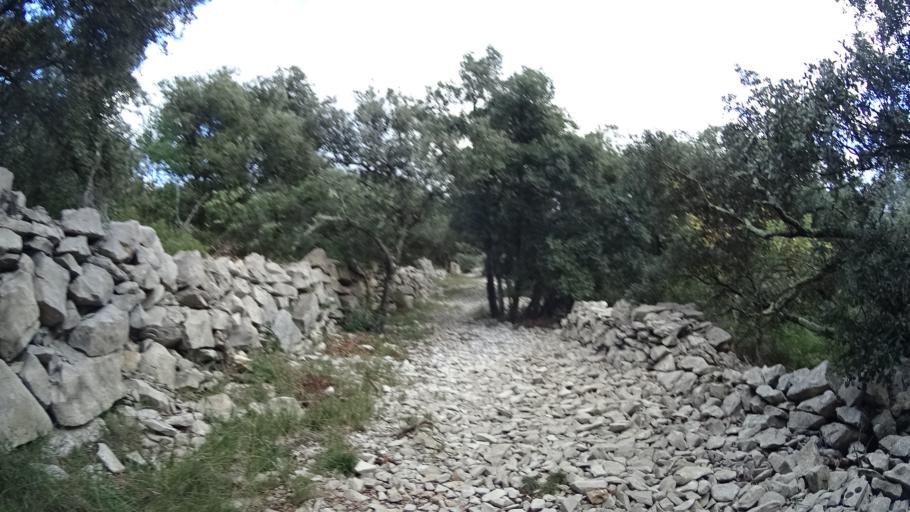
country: FR
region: Languedoc-Roussillon
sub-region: Departement de l'Herault
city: Claret
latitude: 43.8646
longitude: 3.9137
